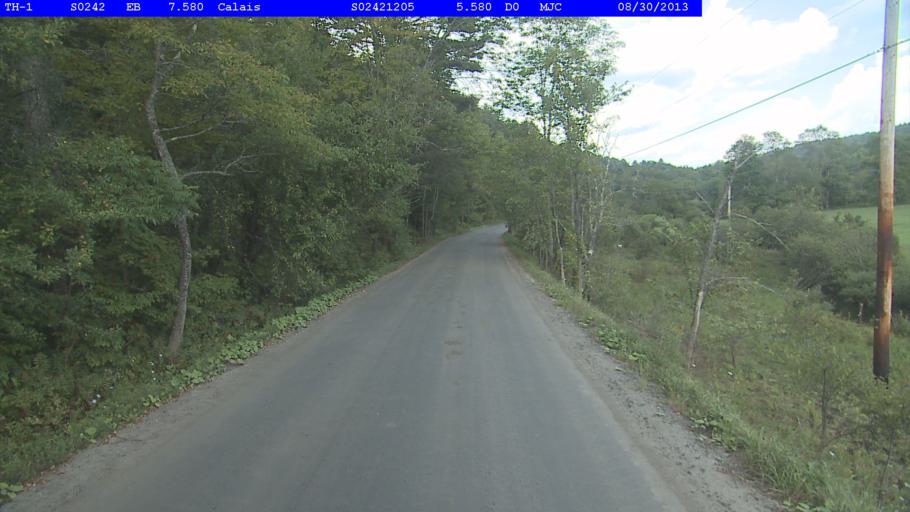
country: US
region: Vermont
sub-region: Caledonia County
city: Hardwick
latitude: 44.3849
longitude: -72.4531
